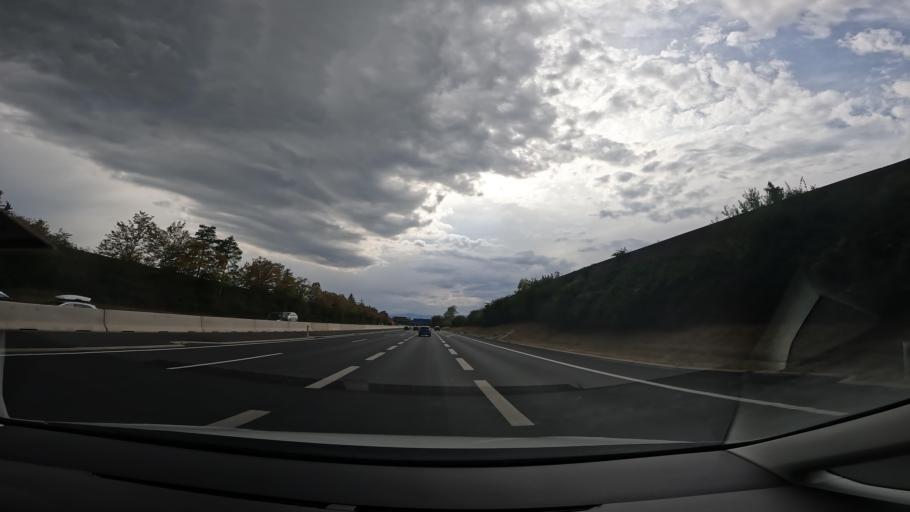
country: AT
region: Styria
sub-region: Politischer Bezirk Graz-Umgebung
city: Seiersberg
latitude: 47.0042
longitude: 15.4209
